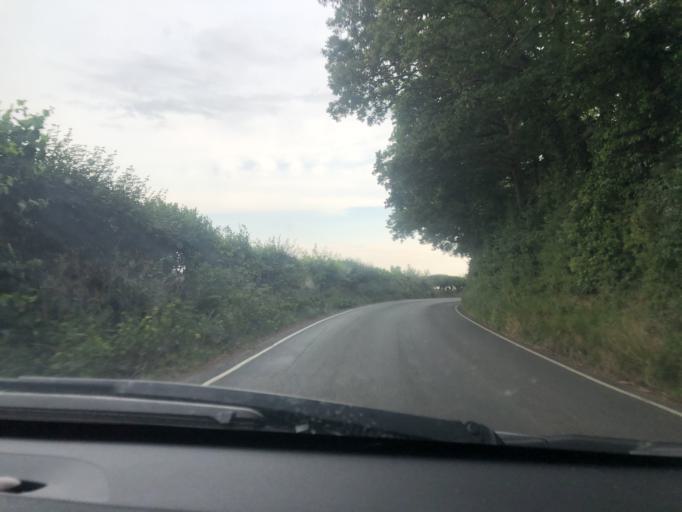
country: GB
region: England
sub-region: Kent
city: Sturry
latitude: 51.3262
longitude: 1.1464
